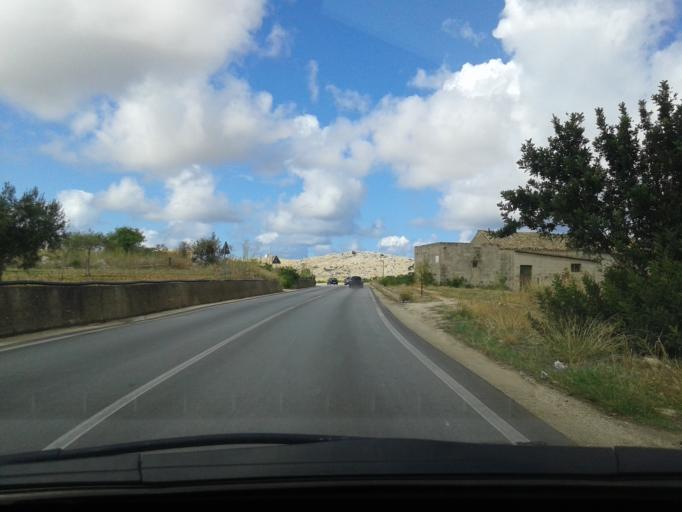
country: IT
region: Sicily
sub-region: Trapani
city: Custonaci
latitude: 38.0800
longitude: 12.7083
